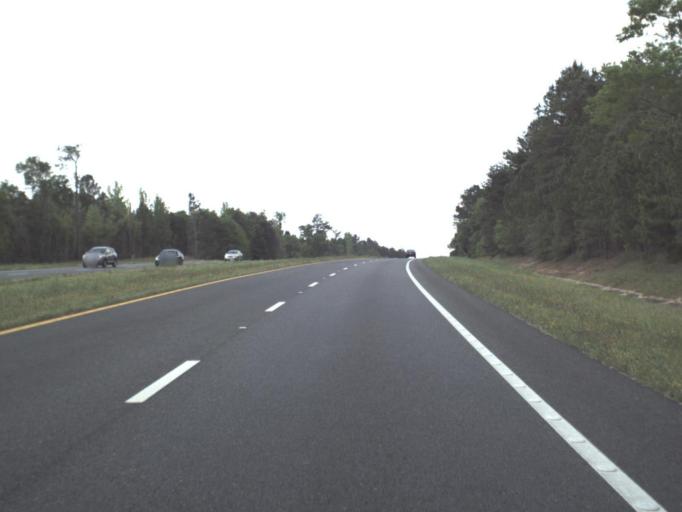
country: US
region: Florida
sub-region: Escambia County
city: Molino
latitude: 30.8539
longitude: -87.3228
